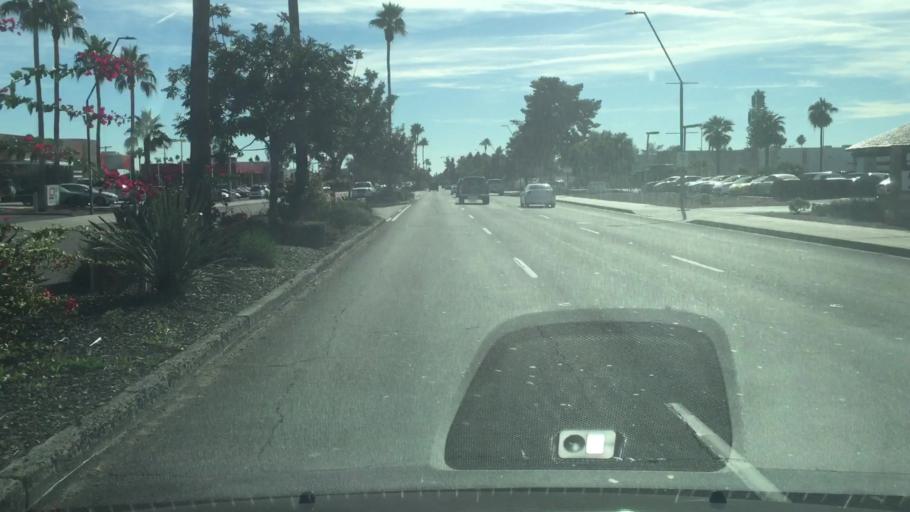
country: US
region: Arizona
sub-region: Maricopa County
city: Tempe
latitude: 33.4575
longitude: -111.9264
